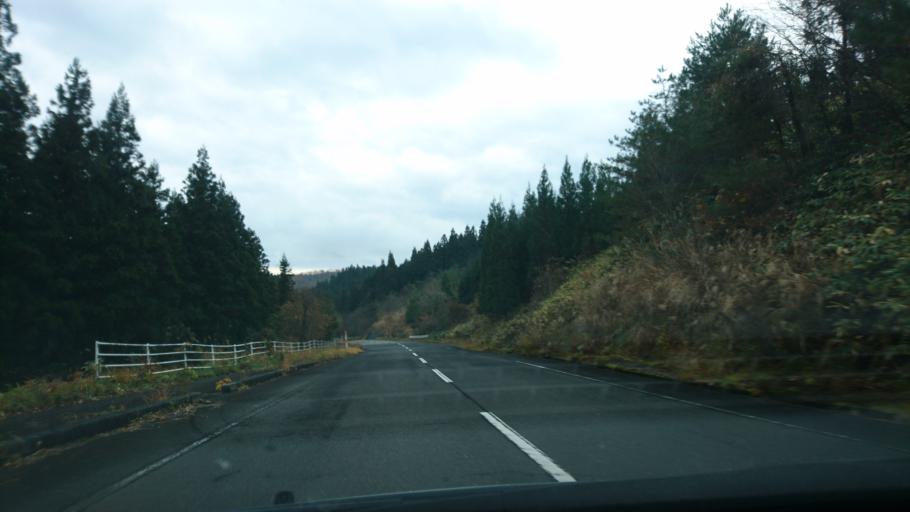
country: JP
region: Iwate
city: Ichinoseki
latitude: 38.9186
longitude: 140.9082
